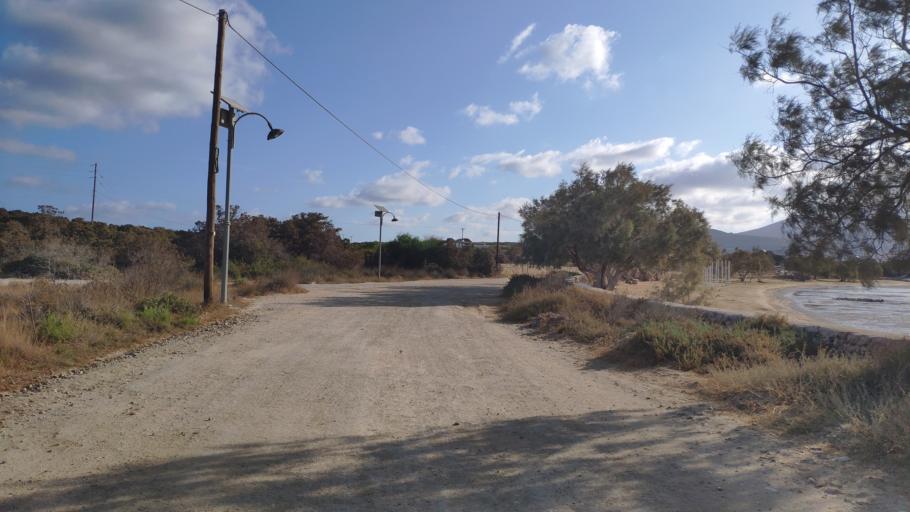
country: GR
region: South Aegean
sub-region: Nomos Kykladon
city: Antiparos
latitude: 37.0441
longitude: 25.0852
